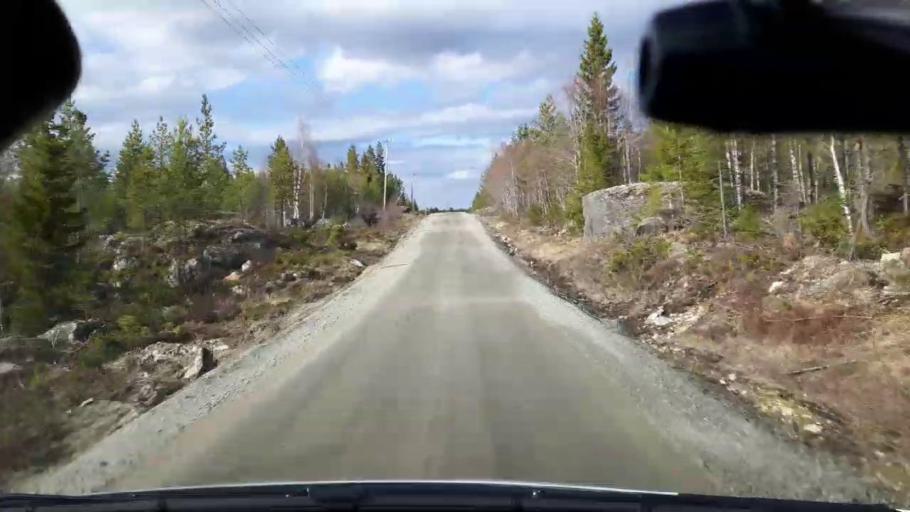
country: SE
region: Jaemtland
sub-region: Bergs Kommun
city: Hoverberg
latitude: 62.8687
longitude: 14.6635
